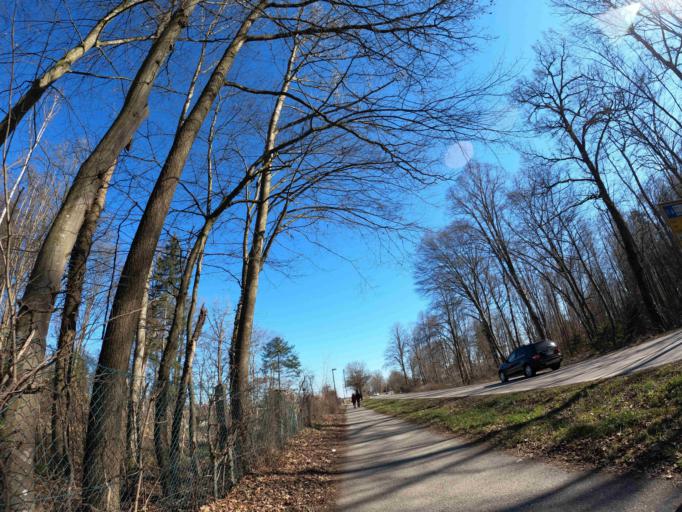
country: DE
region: Bavaria
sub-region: Upper Bavaria
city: Putzbrunn
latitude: 48.0825
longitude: 11.6884
